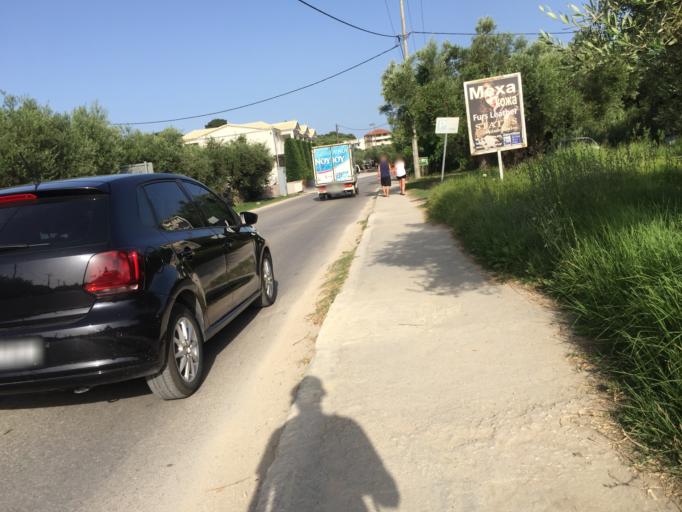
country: GR
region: Ionian Islands
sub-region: Nomos Zakynthou
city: Vanaton
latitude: 37.8192
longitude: 20.8607
